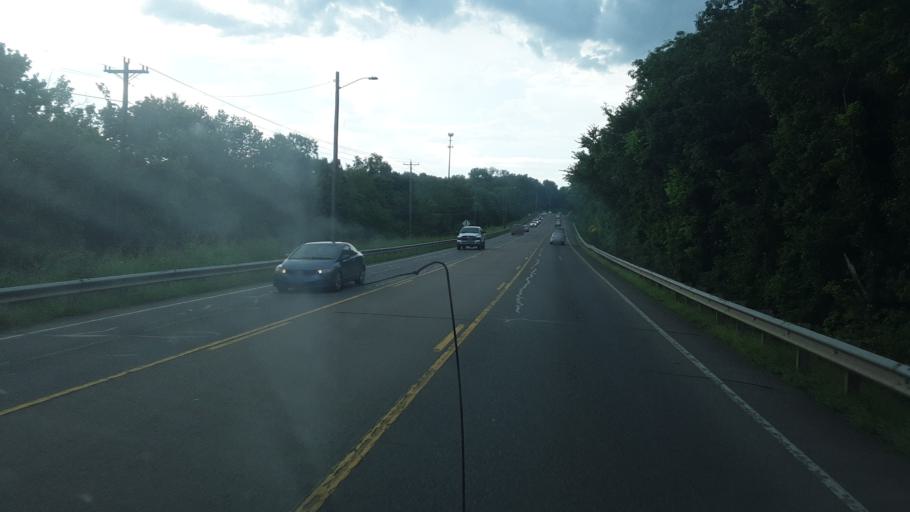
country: US
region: Tennessee
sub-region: Montgomery County
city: Clarksville
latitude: 36.5386
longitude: -87.2852
